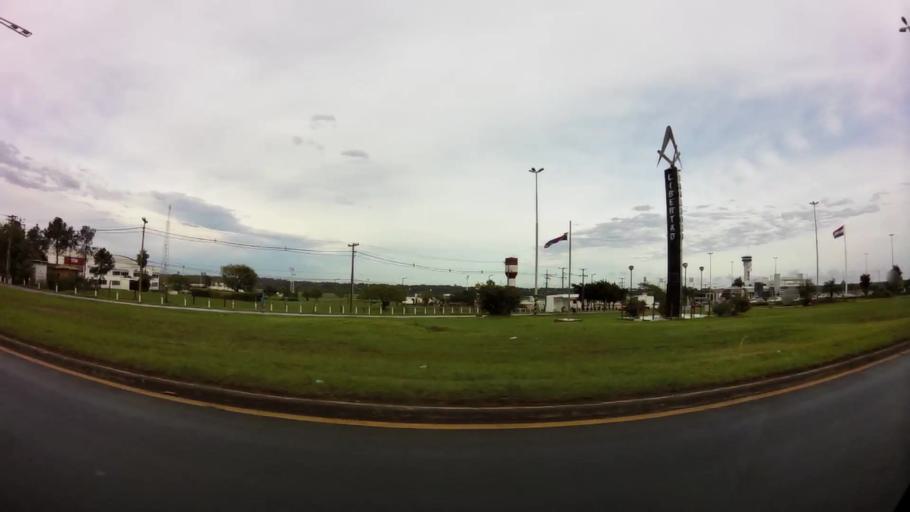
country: PY
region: Central
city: Limpio
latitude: -25.2450
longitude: -57.5113
